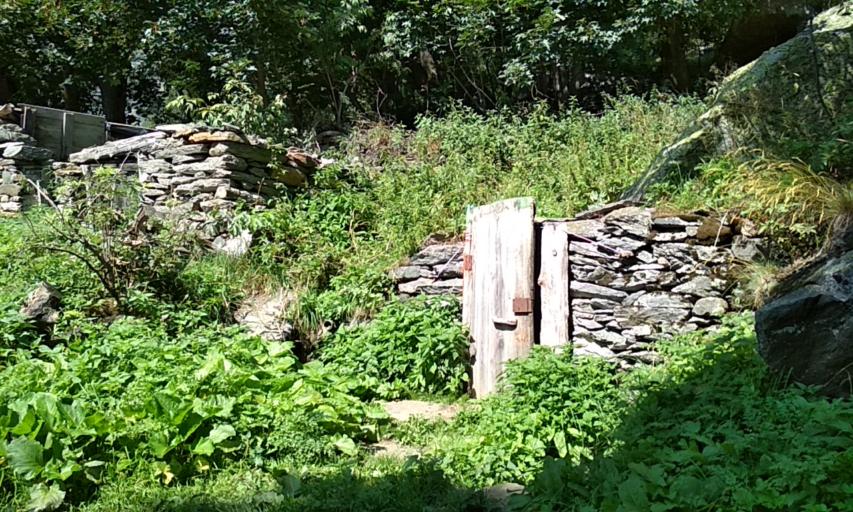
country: IT
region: Piedmont
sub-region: Provincia di Torino
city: Noasca
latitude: 45.4584
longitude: 7.2844
